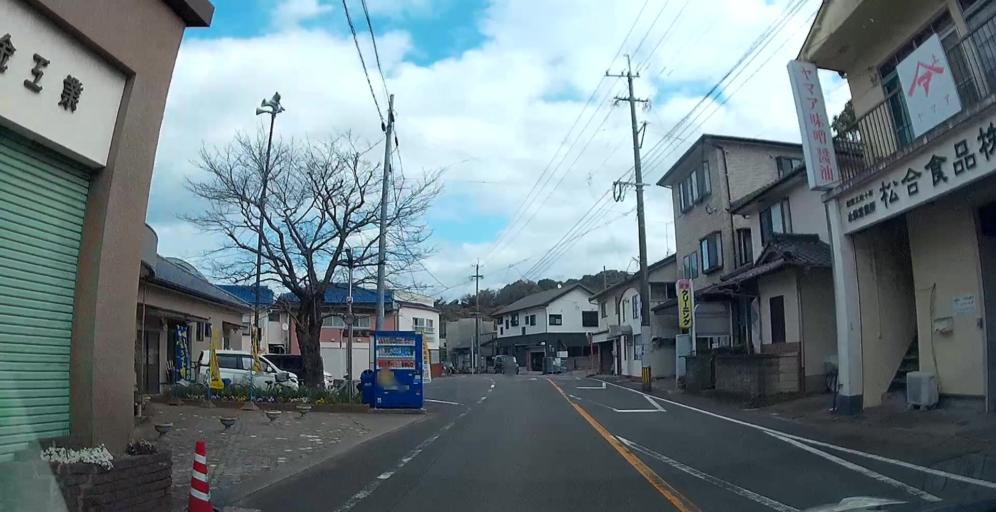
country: JP
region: Kumamoto
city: Minamata
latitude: 32.2012
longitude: 130.3897
